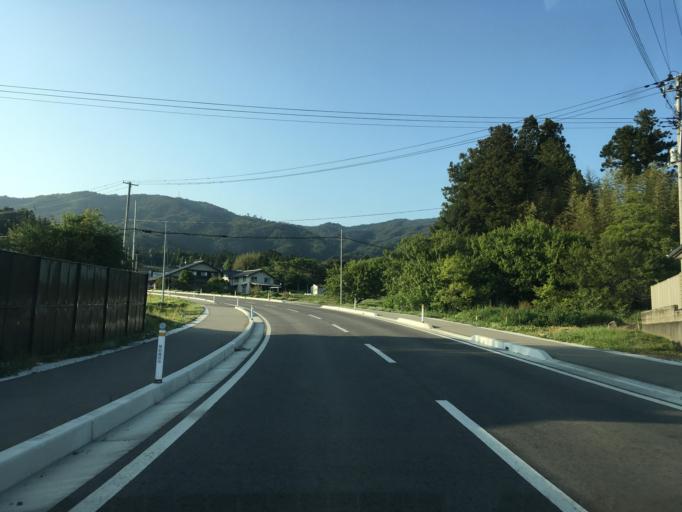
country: JP
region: Iwate
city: Ofunato
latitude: 39.0177
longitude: 141.6669
